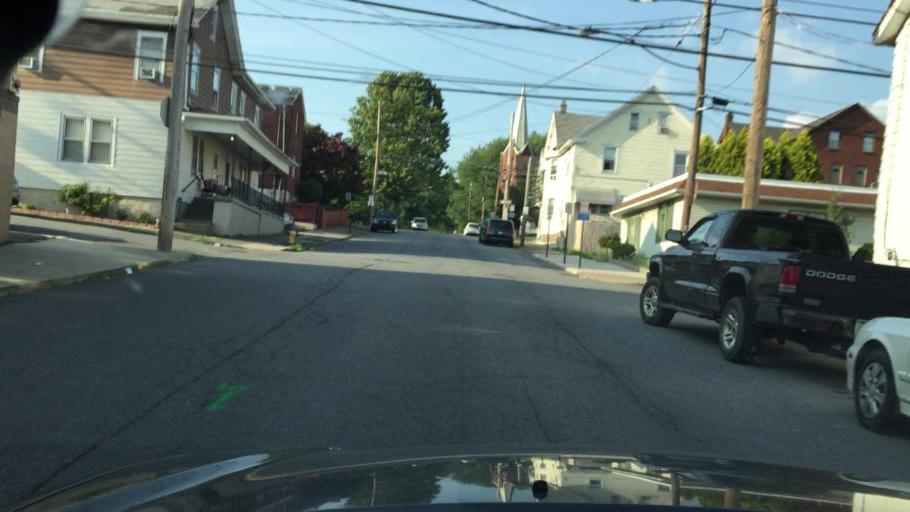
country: US
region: Pennsylvania
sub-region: Luzerne County
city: Hazleton
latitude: 40.9562
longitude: -75.9802
